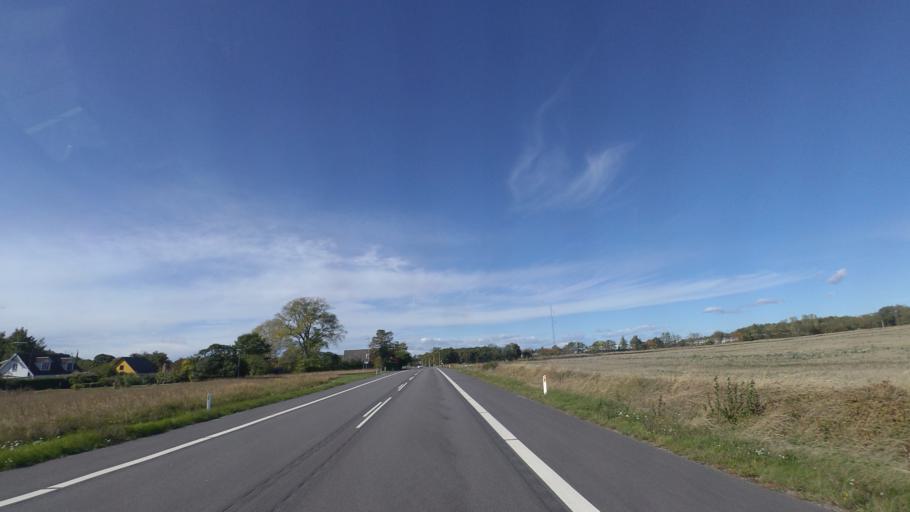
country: DK
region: Capital Region
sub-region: Bornholm Kommune
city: Ronne
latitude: 55.0885
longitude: 14.7410
